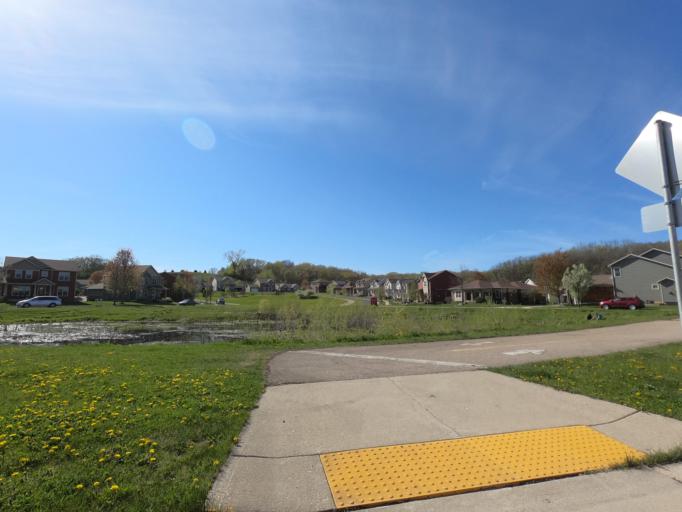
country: US
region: Wisconsin
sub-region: Dane County
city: Middleton
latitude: 43.1027
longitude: -89.5431
